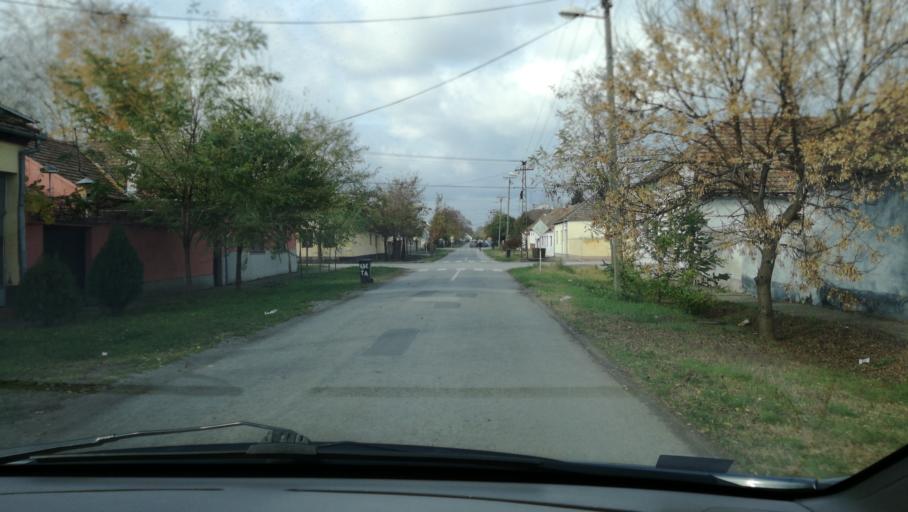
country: RS
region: Autonomna Pokrajina Vojvodina
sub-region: Severnobanatski Okrug
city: Kikinda
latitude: 45.8253
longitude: 20.4565
